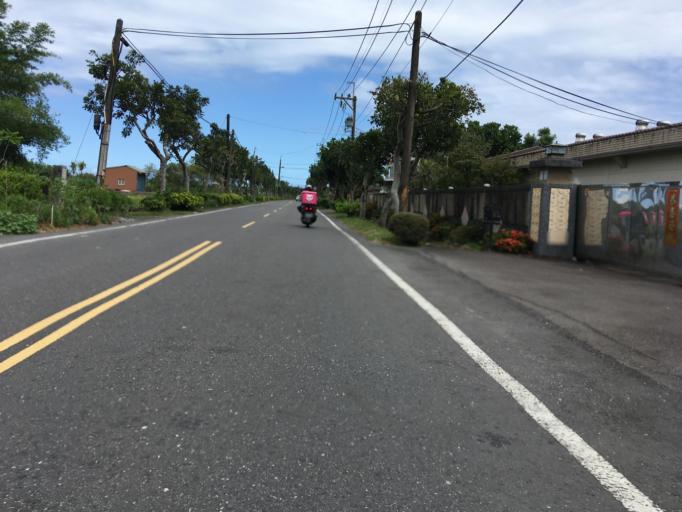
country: TW
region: Taiwan
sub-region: Yilan
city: Yilan
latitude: 24.6845
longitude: 121.8040
